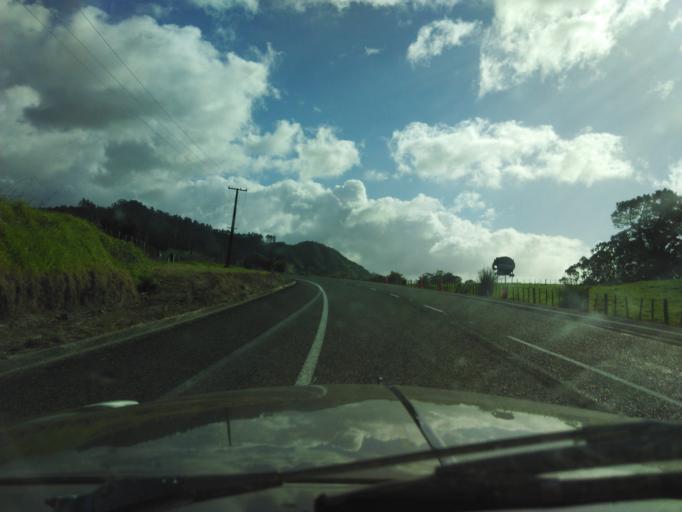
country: NZ
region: Bay of Plenty
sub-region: Western Bay of Plenty District
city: Waihi Beach
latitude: -37.4632
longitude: 175.9367
